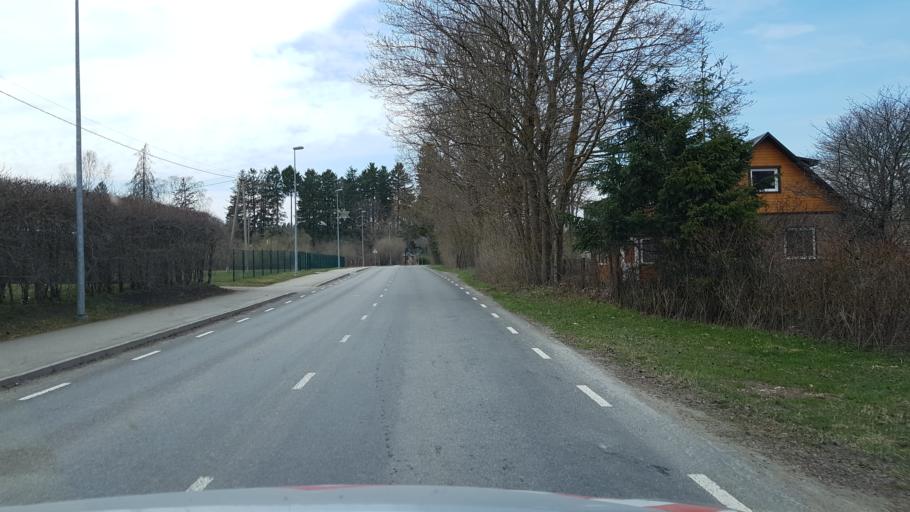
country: EE
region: Laeaene-Virumaa
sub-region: Haljala vald
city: Haljala
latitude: 59.4399
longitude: 26.2605
